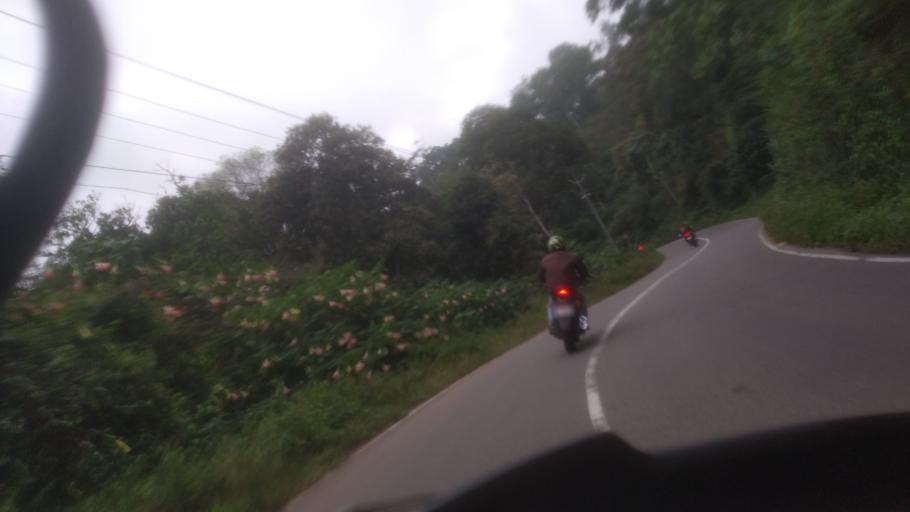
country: IN
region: Tamil Nadu
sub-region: Theni
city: Kombai
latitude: 9.8935
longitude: 77.1666
